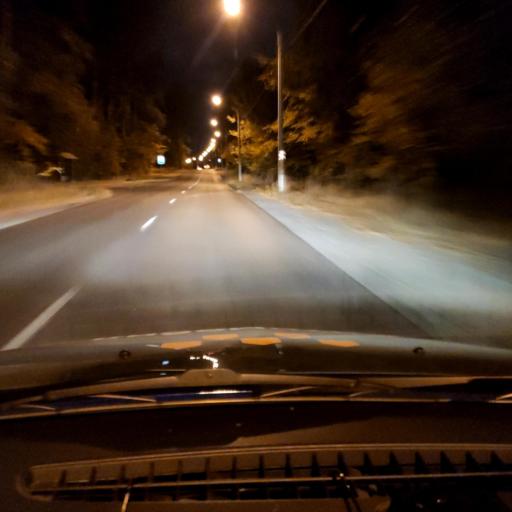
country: RU
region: Voronezj
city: Somovo
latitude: 51.7045
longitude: 39.3247
